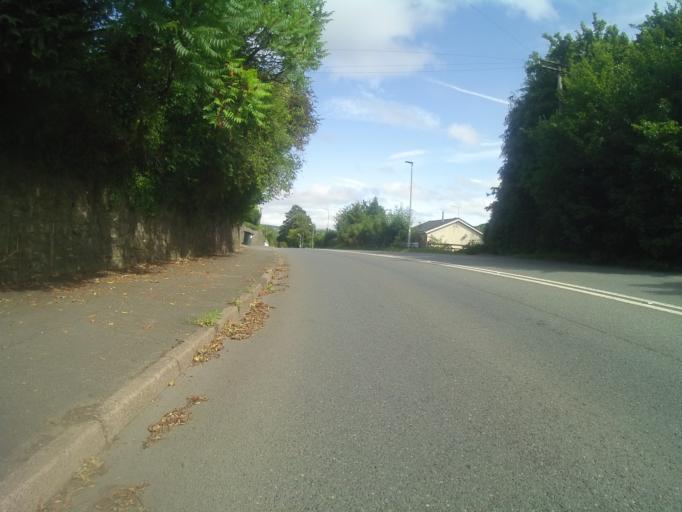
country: GB
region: England
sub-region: Devon
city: Buckfastleigh
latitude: 50.4828
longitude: -3.7706
